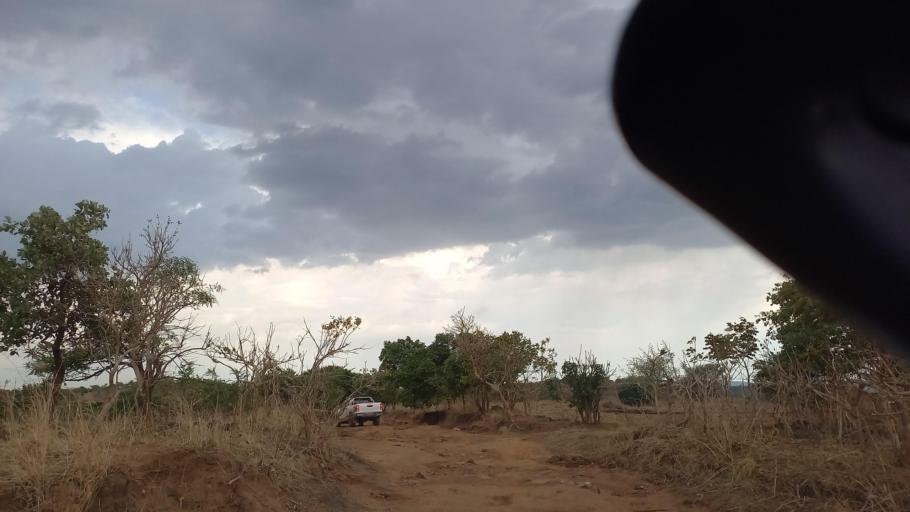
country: ZM
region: Lusaka
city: Kafue
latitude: -16.1279
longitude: 28.0608
